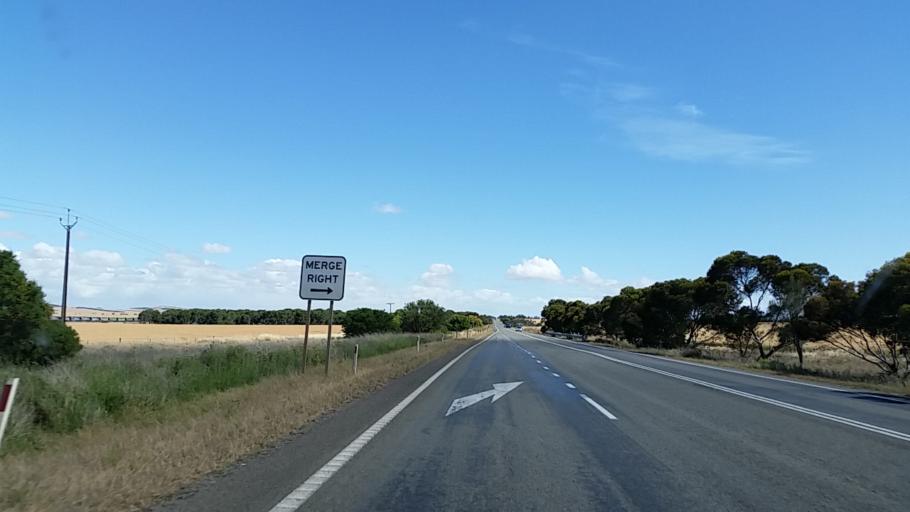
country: AU
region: South Australia
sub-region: Port Pirie City and Dists
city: Crystal Brook
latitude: -33.7170
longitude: 138.2113
